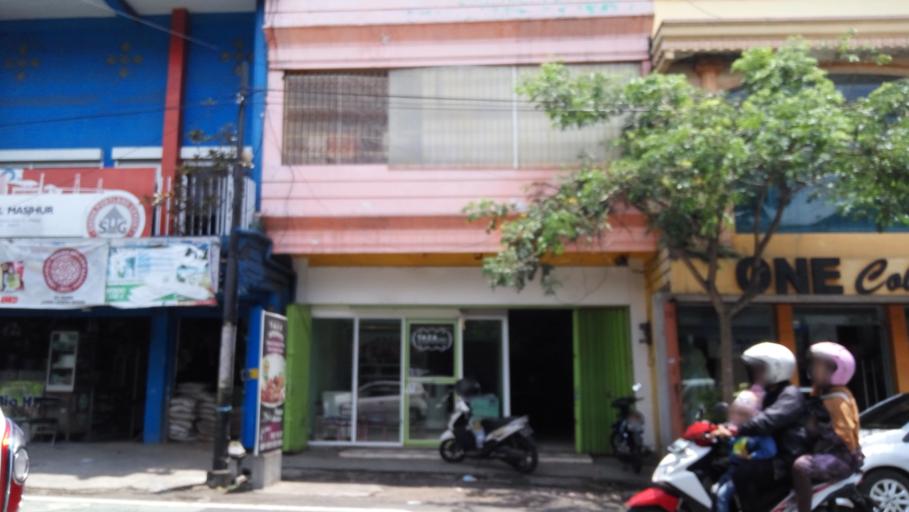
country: ID
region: East Java
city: Malang
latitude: -7.9819
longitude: 112.6272
